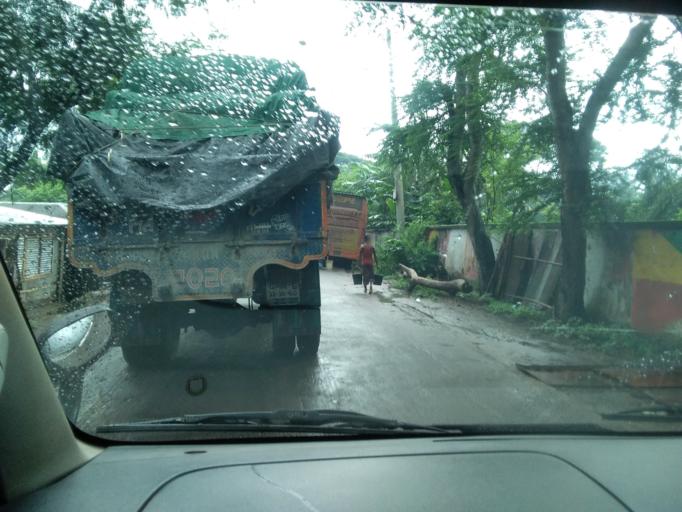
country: IN
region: West Bengal
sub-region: North 24 Parganas
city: Taki
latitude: 22.3468
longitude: 89.1040
